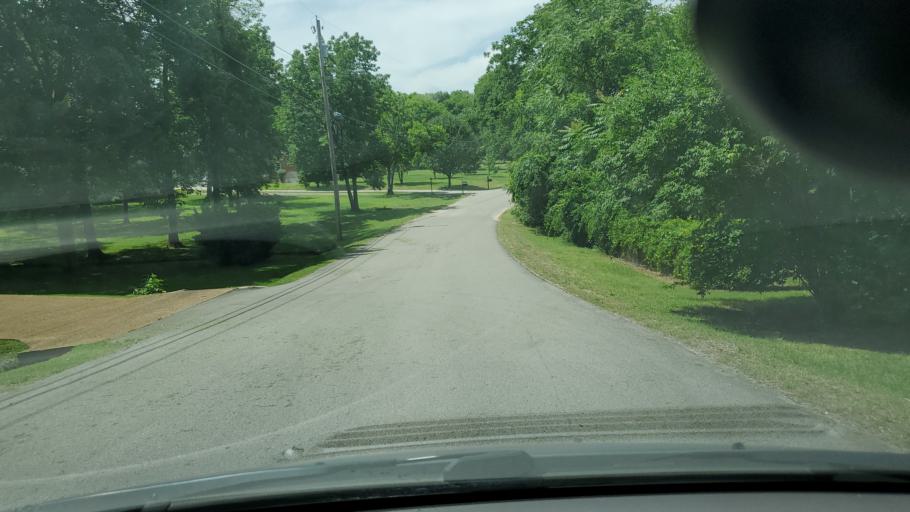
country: US
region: Tennessee
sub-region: Davidson County
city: Nashville
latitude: 36.2342
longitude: -86.7354
